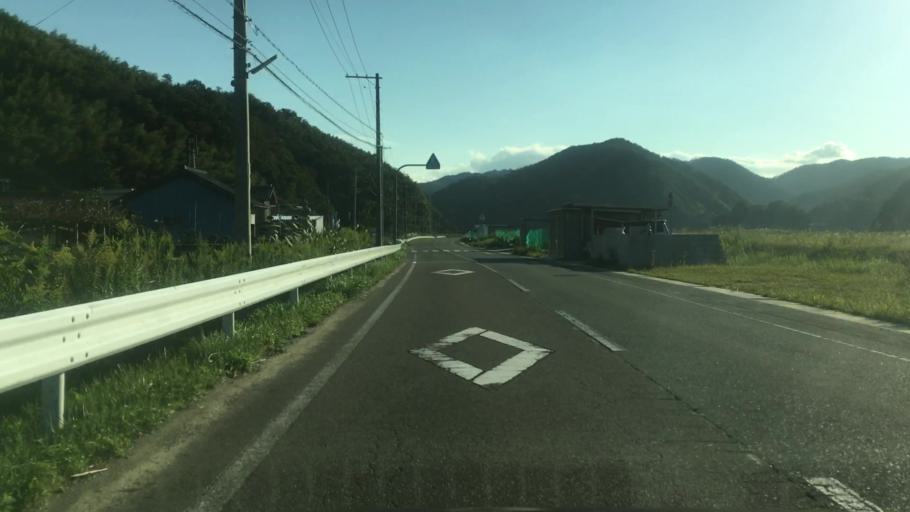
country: JP
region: Hyogo
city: Toyooka
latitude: 35.6136
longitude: 134.8113
